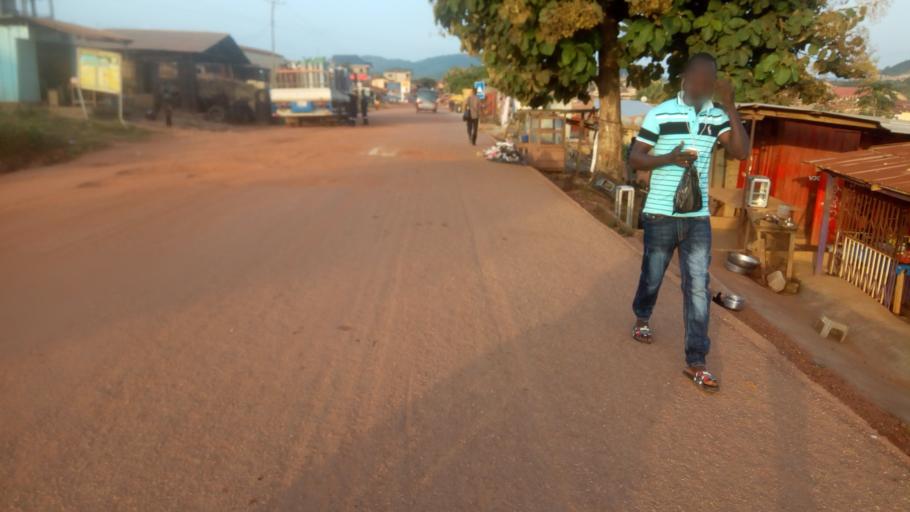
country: GH
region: Ashanti
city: Obuasi
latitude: 6.2125
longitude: -1.6923
